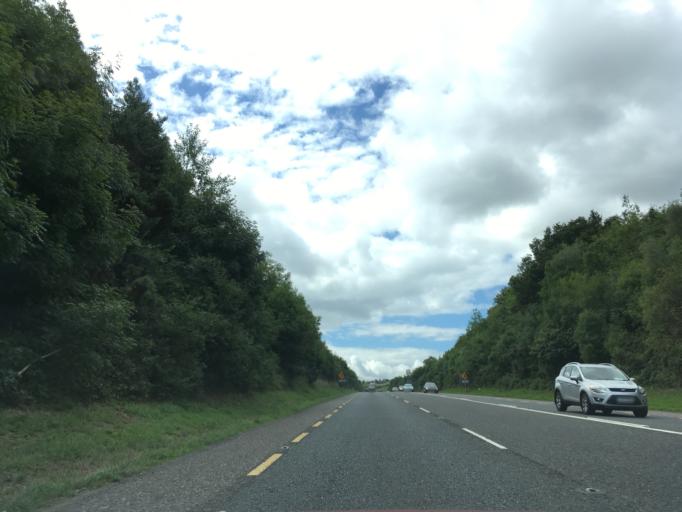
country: IE
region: Munster
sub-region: County Cork
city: Carrigaline
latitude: 51.8661
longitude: -8.4157
